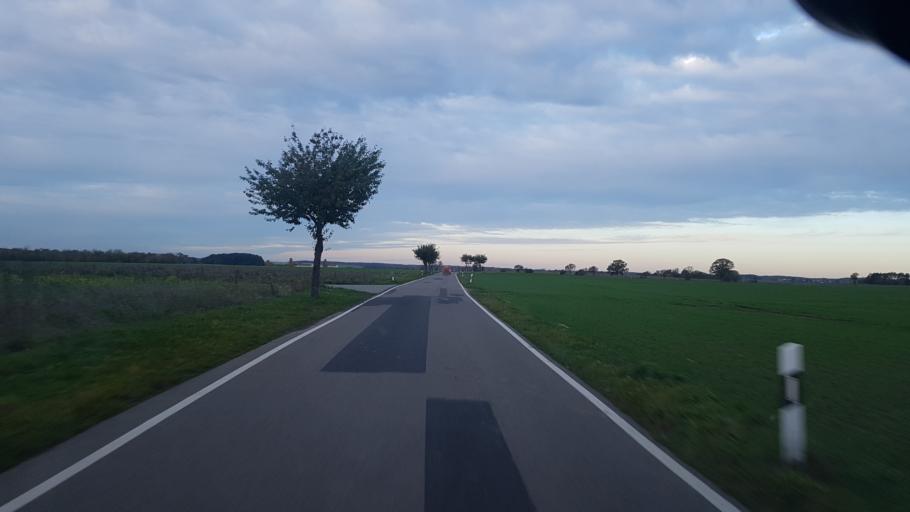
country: DE
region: Saxony
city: Cavertitz
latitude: 51.3922
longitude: 13.1542
